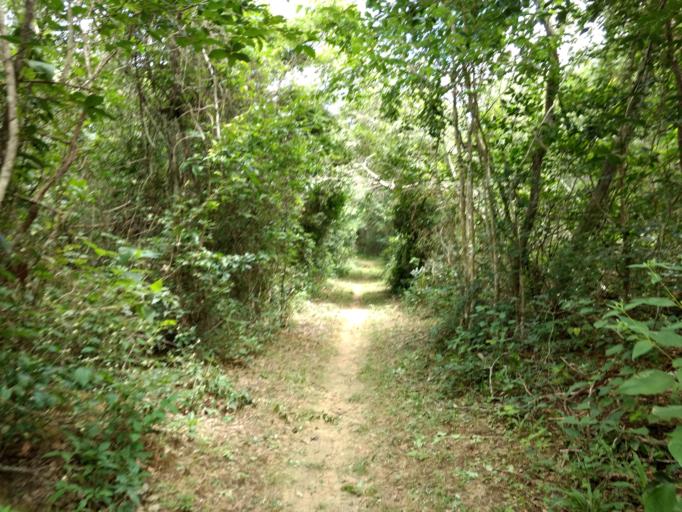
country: BR
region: Ceara
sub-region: Crateus
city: Crateus
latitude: -5.1570
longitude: -40.8965
